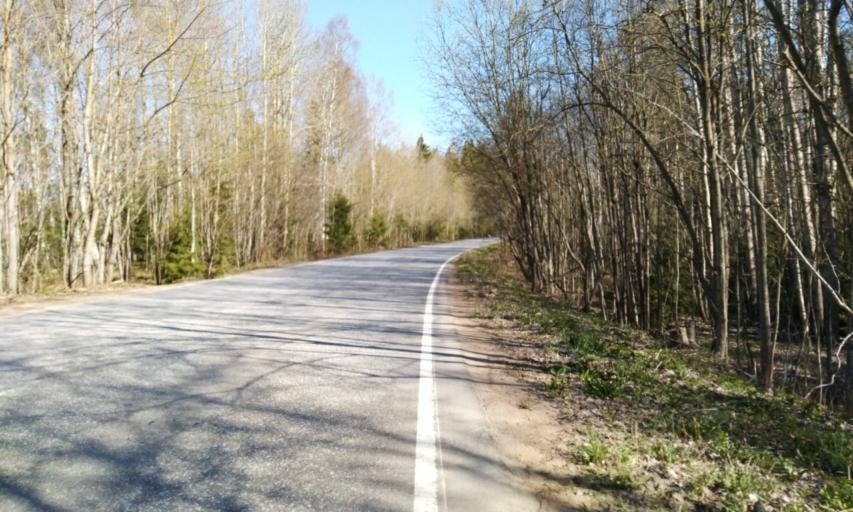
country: RU
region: Leningrad
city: Garbolovo
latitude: 60.3682
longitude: 30.4406
